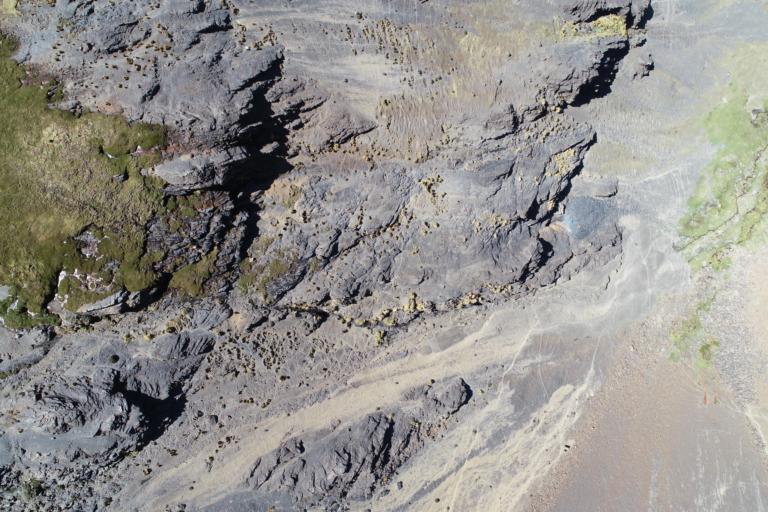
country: BO
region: La Paz
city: La Paz
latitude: -16.6185
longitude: -67.8241
